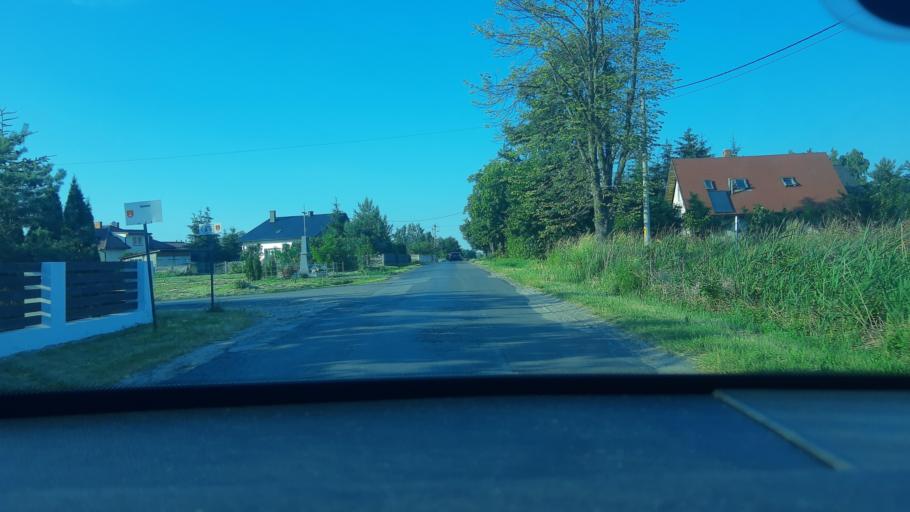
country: PL
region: Lodz Voivodeship
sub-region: Powiat sieradzki
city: Sieradz
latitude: 51.5483
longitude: 18.7567
